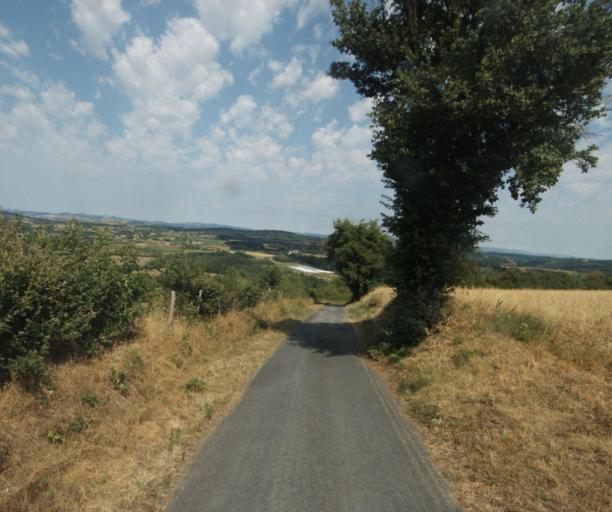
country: FR
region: Rhone-Alpes
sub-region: Departement du Rhone
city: Lentilly
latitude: 45.8424
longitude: 4.6481
